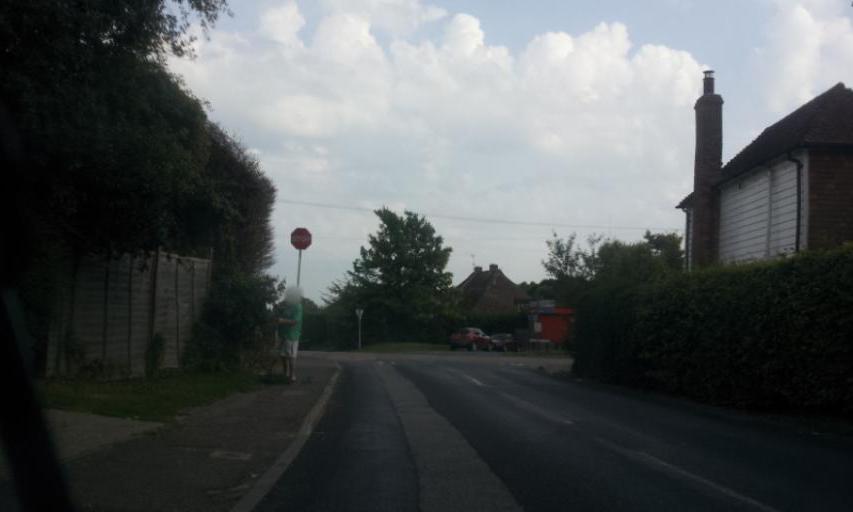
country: GB
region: England
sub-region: Kent
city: Paddock Wood
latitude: 51.1540
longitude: 0.3730
